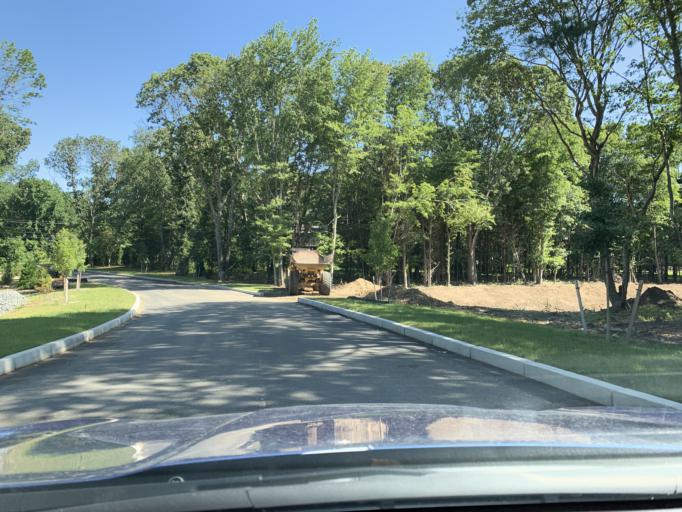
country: US
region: Rhode Island
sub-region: Washington County
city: Exeter
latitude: 41.6233
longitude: -71.5151
